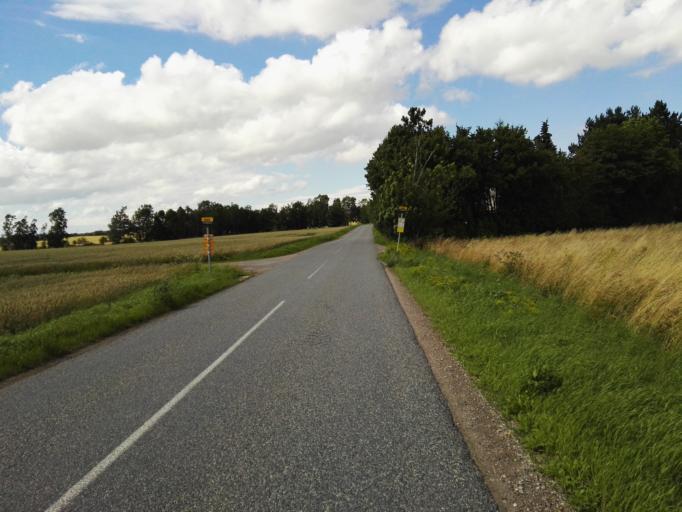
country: DK
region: Capital Region
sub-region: Egedal Kommune
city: Ganlose
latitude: 55.7910
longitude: 12.2315
